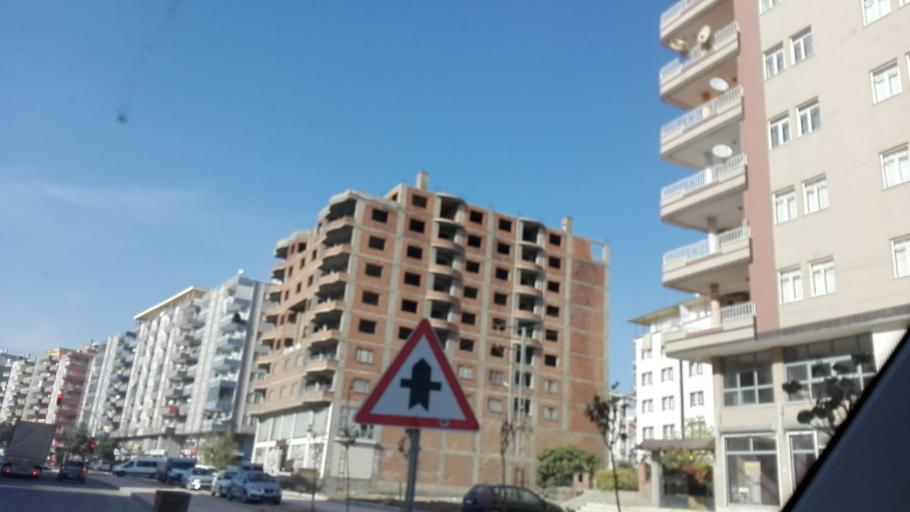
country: TR
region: Batman
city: Aydinkonak
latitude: 37.8998
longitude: 41.1463
